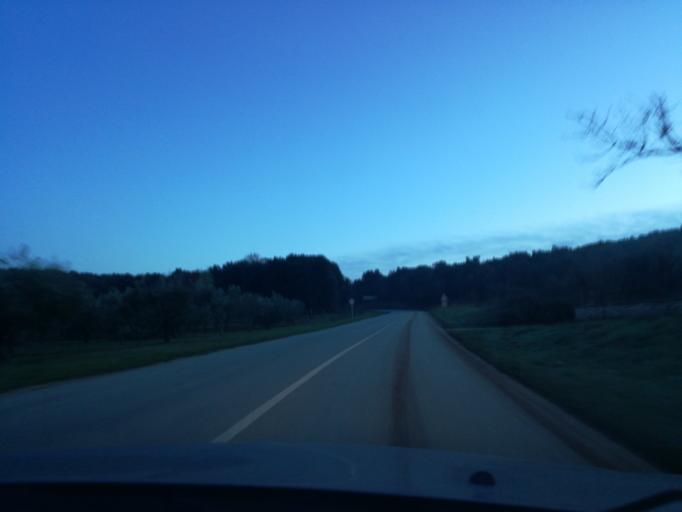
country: HR
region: Istarska
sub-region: Grad Rovinj
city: Rovinj
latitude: 45.1079
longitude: 13.6372
